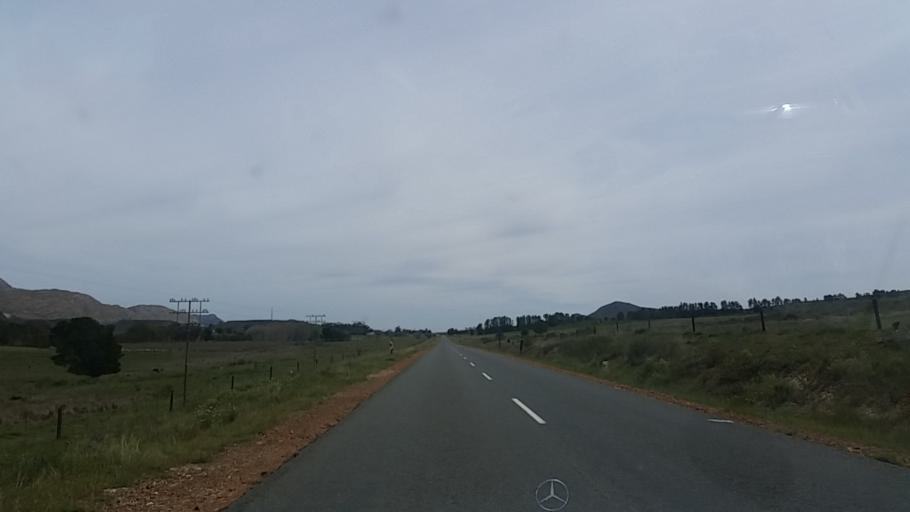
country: ZA
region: Western Cape
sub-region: Eden District Municipality
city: Knysna
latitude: -33.7664
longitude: 22.8129
